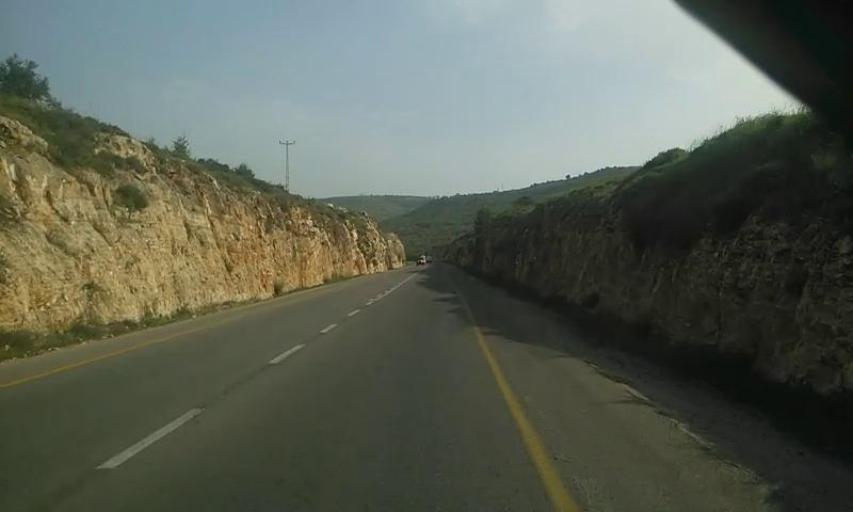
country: PS
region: West Bank
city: Jit
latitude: 32.2279
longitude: 35.1722
